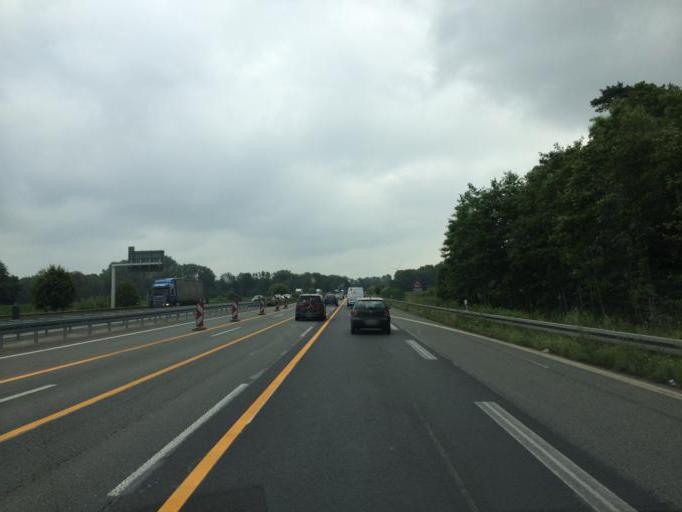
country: DE
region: North Rhine-Westphalia
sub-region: Regierungsbezirk Detmold
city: Guetersloh
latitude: 51.8673
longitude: 8.3758
